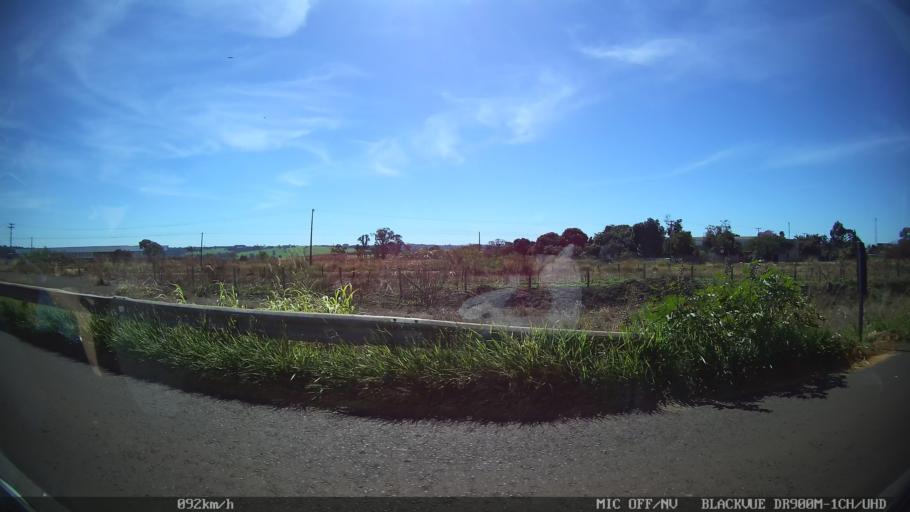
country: BR
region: Sao Paulo
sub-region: Franca
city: Franca
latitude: -20.5460
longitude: -47.4704
